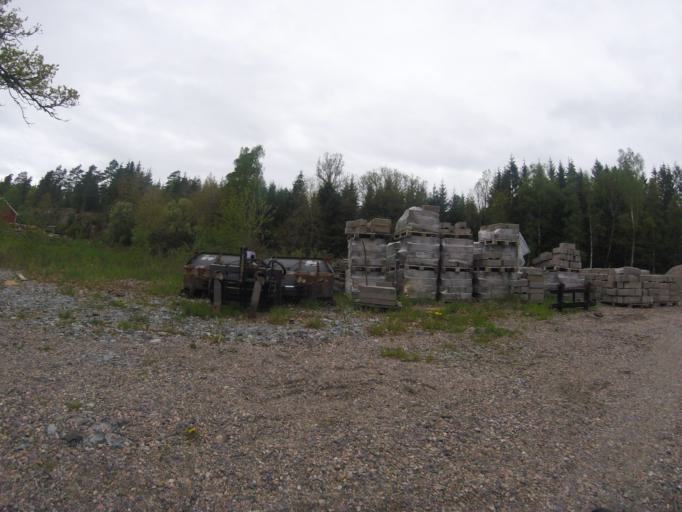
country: SE
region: Vaestra Goetaland
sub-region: Alingsas Kommun
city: Alingsas
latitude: 57.8962
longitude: 12.5622
